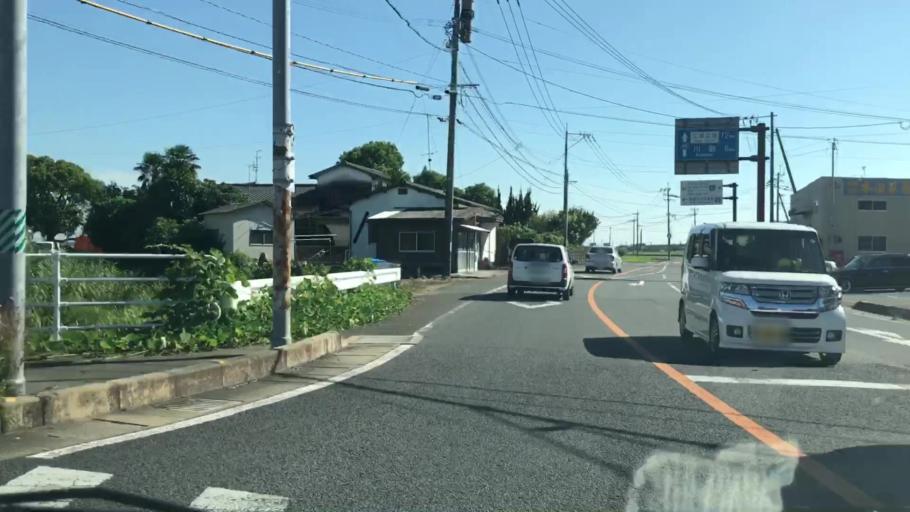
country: JP
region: Saga Prefecture
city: Okawa
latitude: 33.2234
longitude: 130.3516
